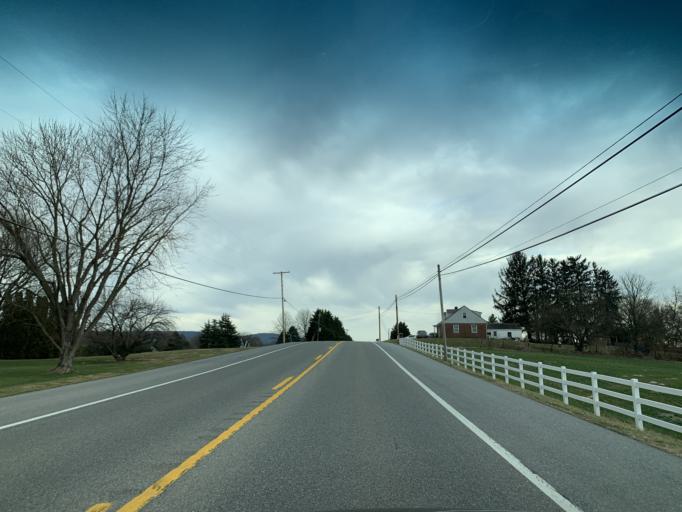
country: US
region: Maryland
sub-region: Washington County
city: Boonsboro
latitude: 39.5587
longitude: -77.6835
